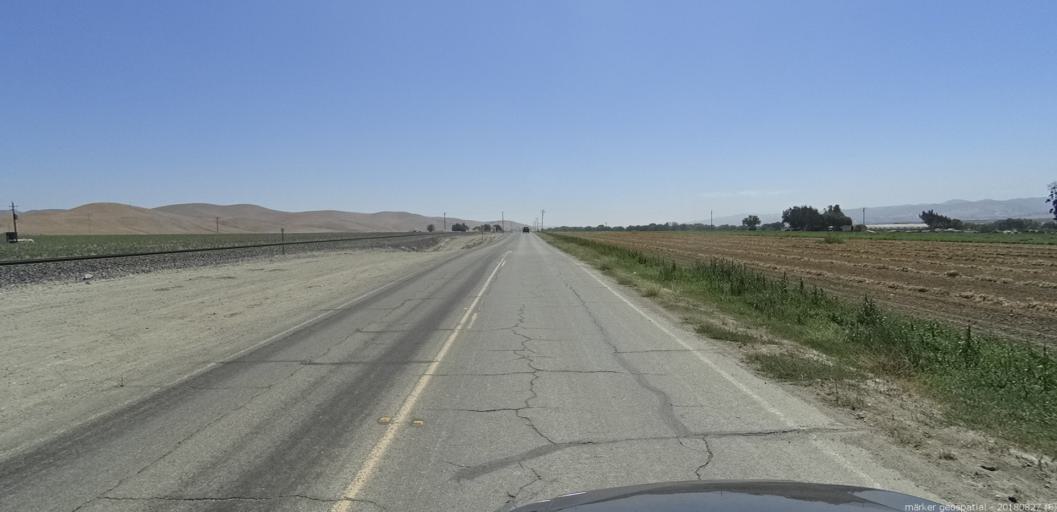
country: US
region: California
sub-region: Monterey County
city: King City
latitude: 36.0740
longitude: -120.9381
